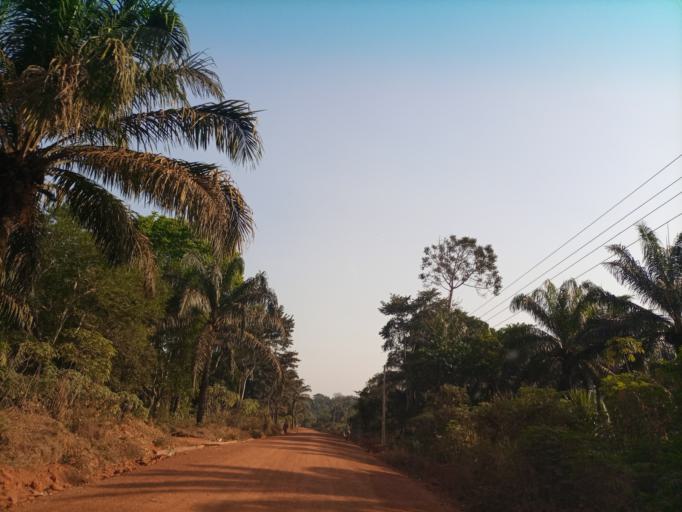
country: NG
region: Enugu
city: Opi
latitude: 6.7701
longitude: 7.3921
